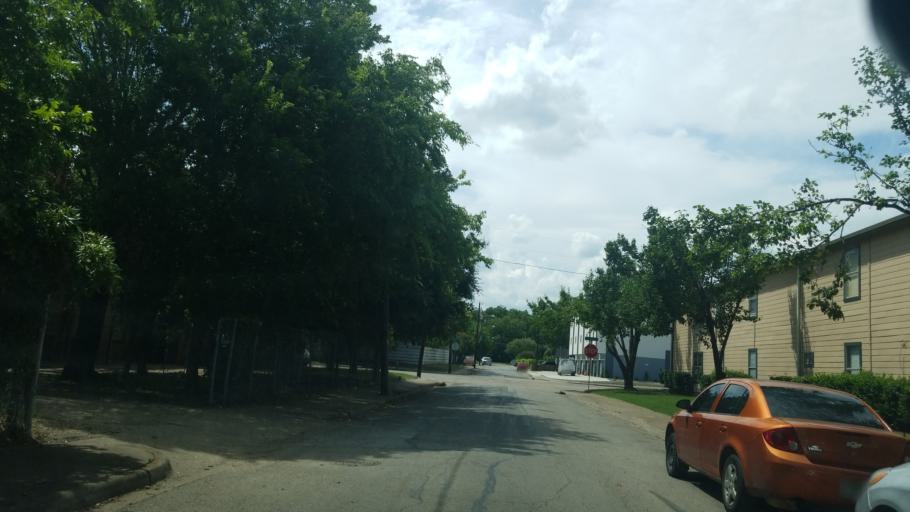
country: US
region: Texas
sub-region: Dallas County
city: Dallas
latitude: 32.7931
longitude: -96.7652
